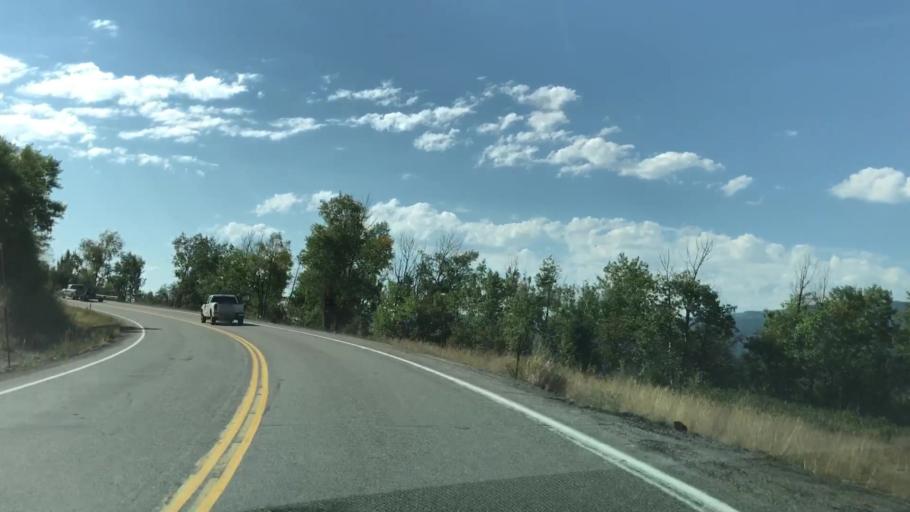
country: US
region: Idaho
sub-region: Teton County
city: Victor
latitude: 43.3143
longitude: -111.1466
